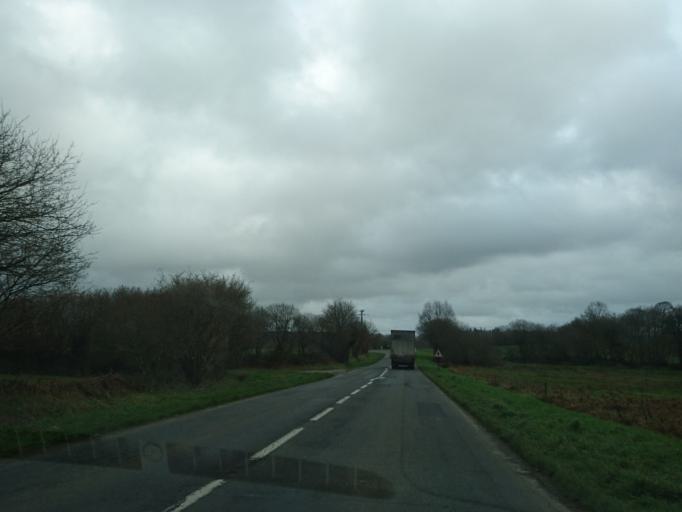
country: FR
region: Brittany
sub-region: Departement des Cotes-d'Armor
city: Rostrenen
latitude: 48.2131
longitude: -3.3267
